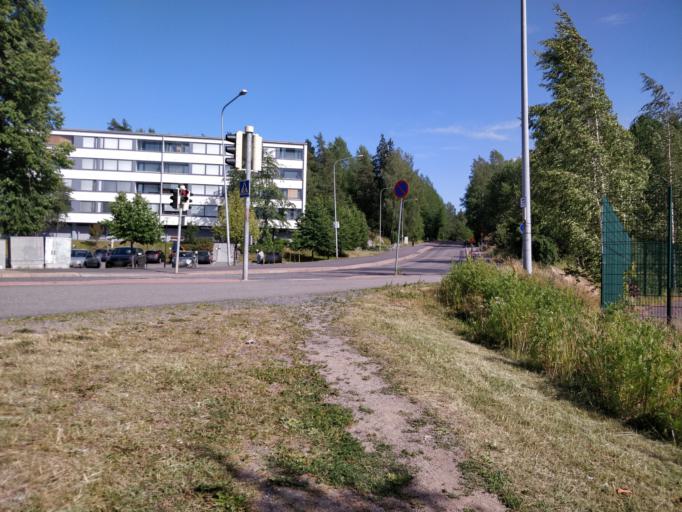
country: FI
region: Uusimaa
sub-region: Helsinki
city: Vantaa
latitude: 60.2393
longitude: 25.0020
